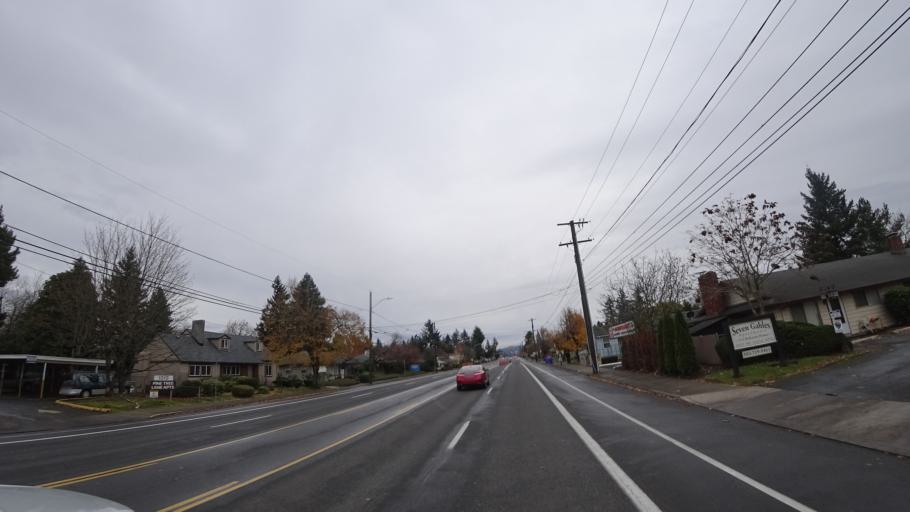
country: US
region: Oregon
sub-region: Multnomah County
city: Lents
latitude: 45.5159
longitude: -122.5378
